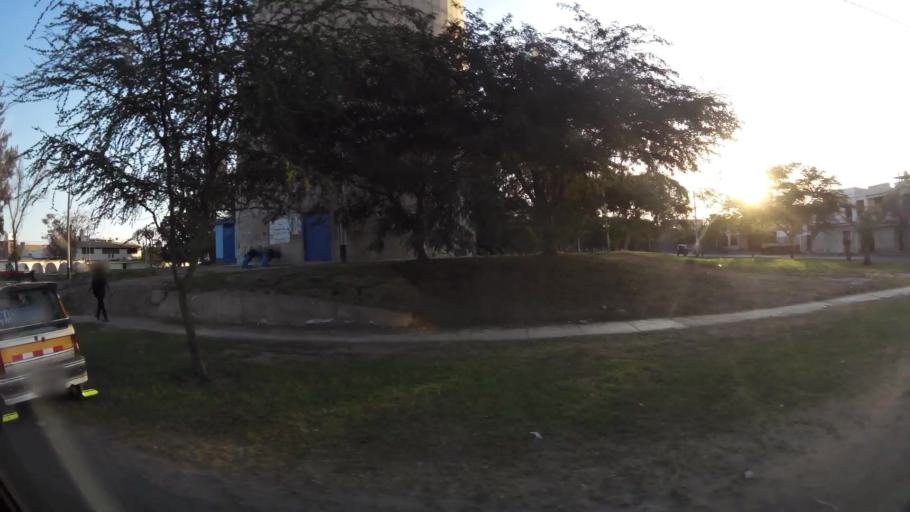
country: PE
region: Ica
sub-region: Provincia de Ica
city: Ica
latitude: -14.0761
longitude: -75.7233
